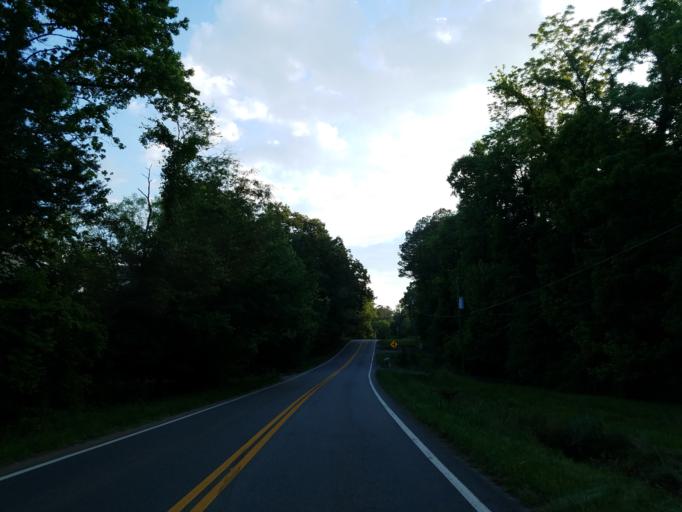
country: US
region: Georgia
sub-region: Cherokee County
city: Canton
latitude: 34.2139
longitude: -84.5082
